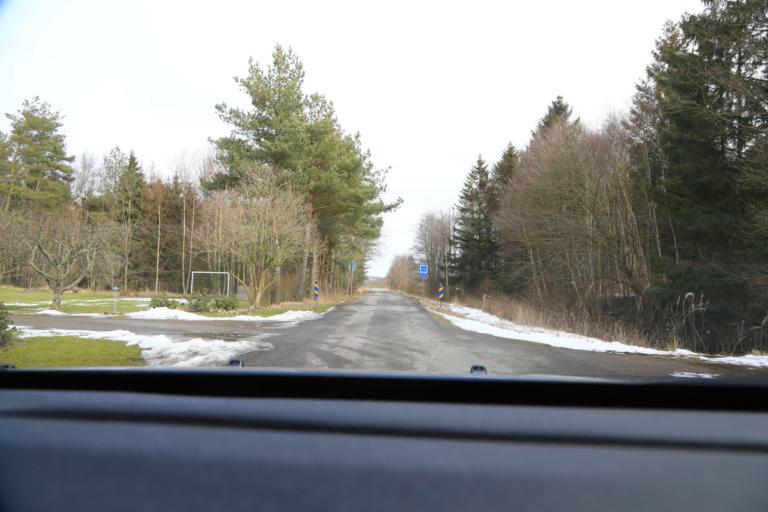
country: SE
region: Halland
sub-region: Varbergs Kommun
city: Veddige
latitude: 57.2059
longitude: 12.2380
